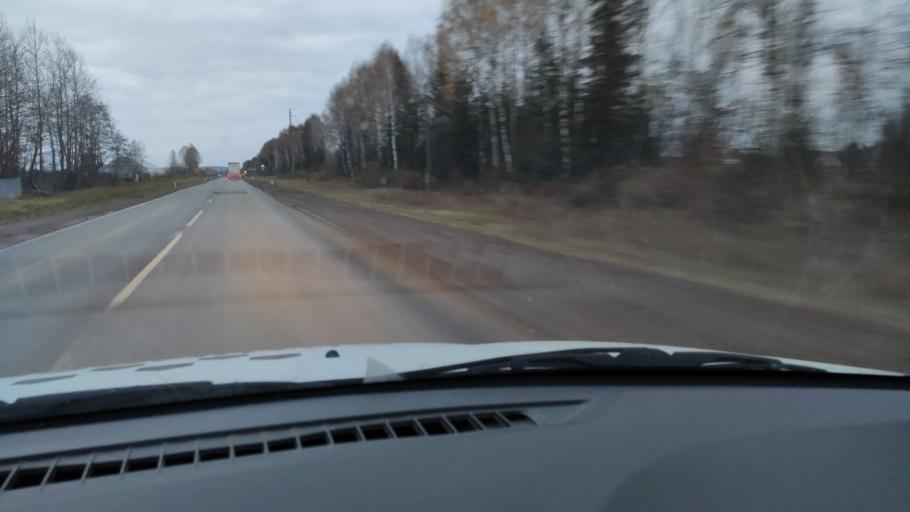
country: RU
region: Kirov
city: Kostino
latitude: 58.8594
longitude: 53.1765
